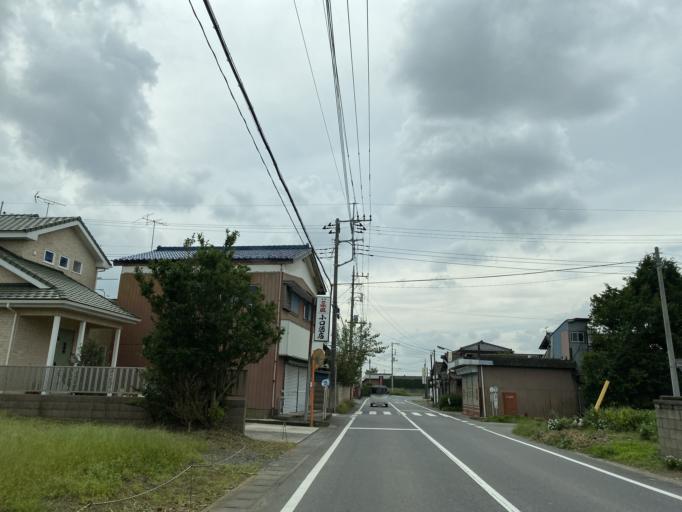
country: JP
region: Ibaraki
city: Moriya
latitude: 35.9707
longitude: 140.0314
